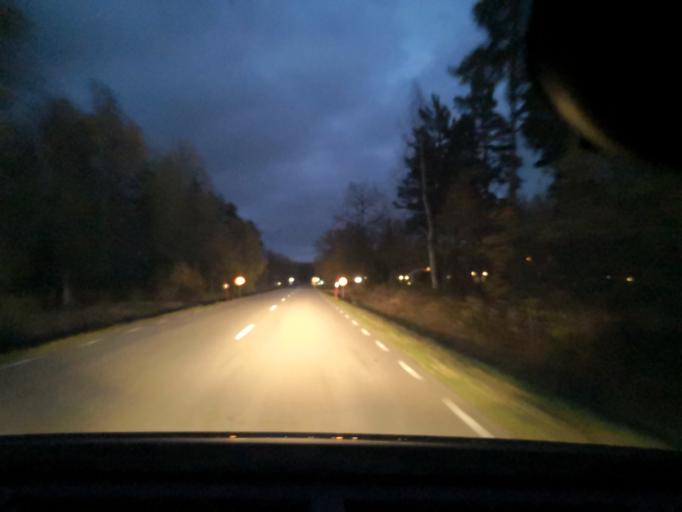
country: SE
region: Uppsala
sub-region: Enkopings Kommun
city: Hummelsta
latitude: 59.5709
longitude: 16.8617
